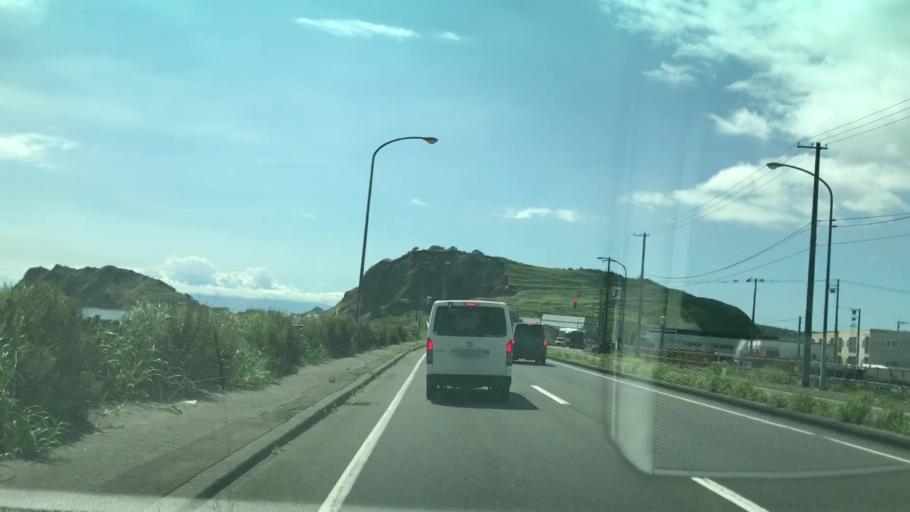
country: JP
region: Hokkaido
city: Muroran
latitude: 42.3454
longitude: 141.0370
